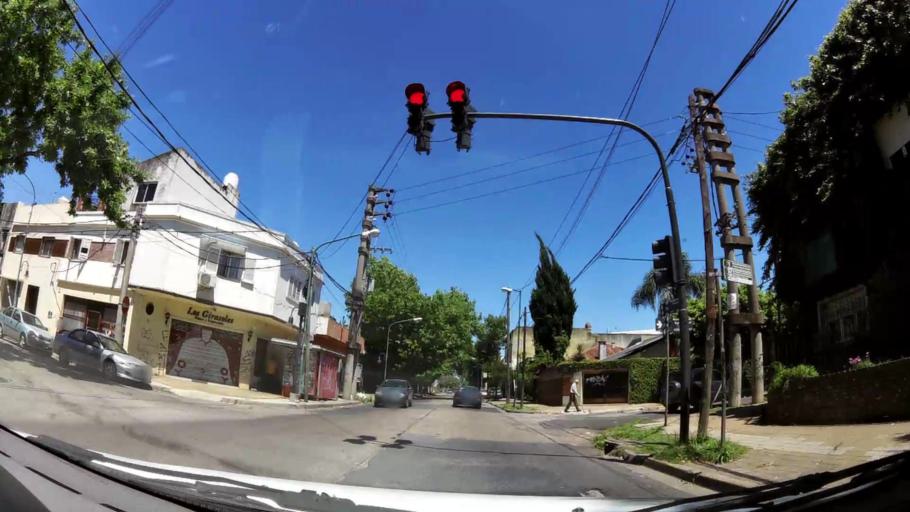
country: AR
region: Buenos Aires
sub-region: Partido de Vicente Lopez
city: Olivos
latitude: -34.4999
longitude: -58.5024
